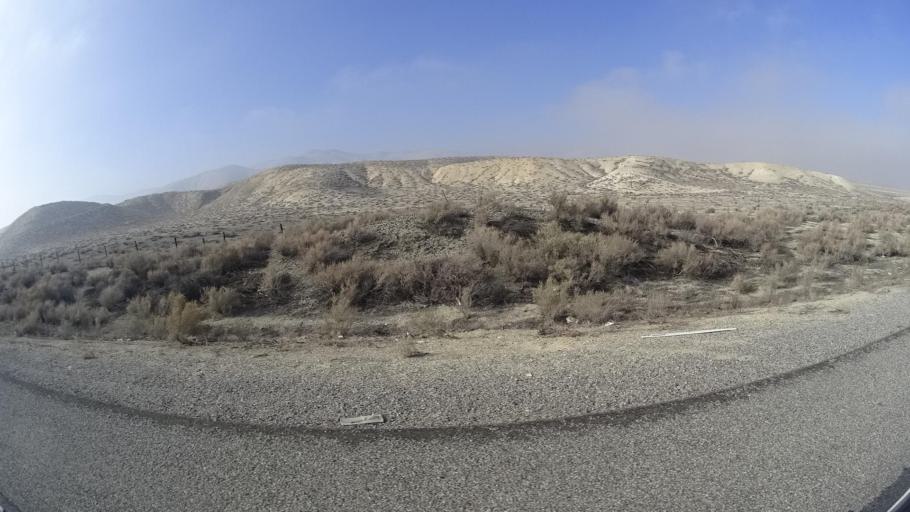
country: US
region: California
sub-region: Kern County
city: Maricopa
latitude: 35.0420
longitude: -119.4228
